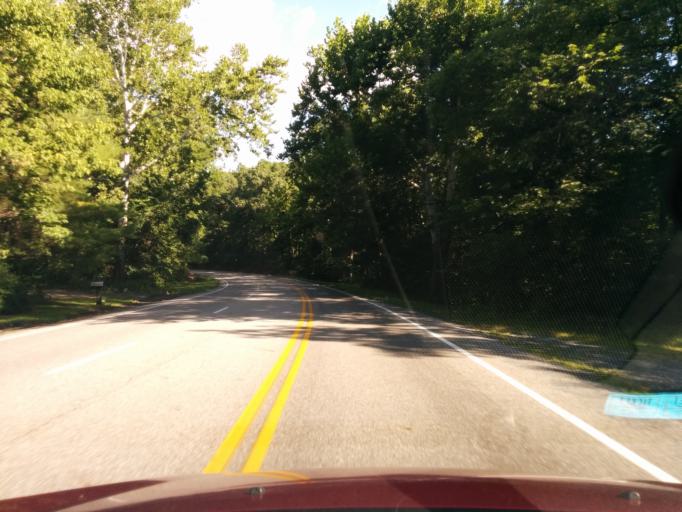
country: US
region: Virginia
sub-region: Rockbridge County
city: Glasgow
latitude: 37.7078
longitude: -79.4660
